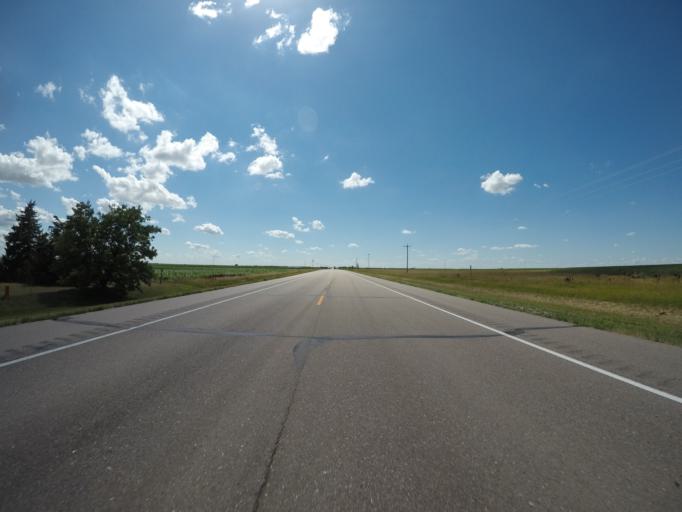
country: US
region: Nebraska
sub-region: Chase County
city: Imperial
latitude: 40.4952
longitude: -101.5488
